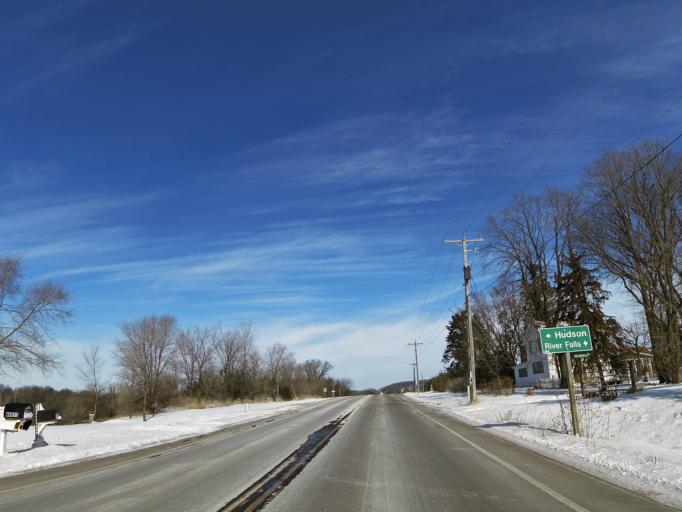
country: US
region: Minnesota
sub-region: Washington County
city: Afton
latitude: 44.8608
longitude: -92.7312
